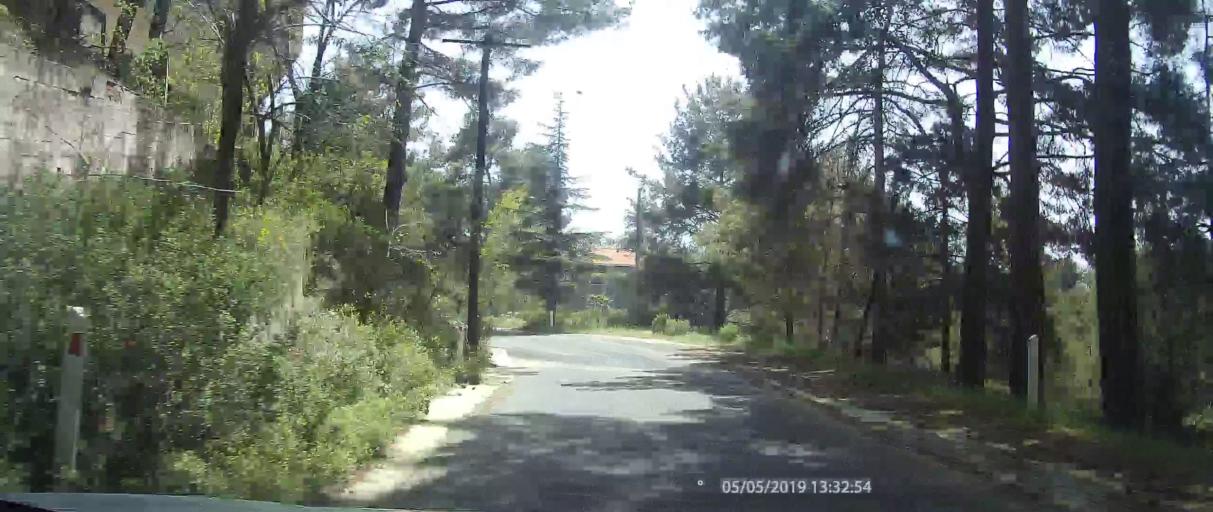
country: CY
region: Lefkosia
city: Kakopetria
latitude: 34.8881
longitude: 32.8547
